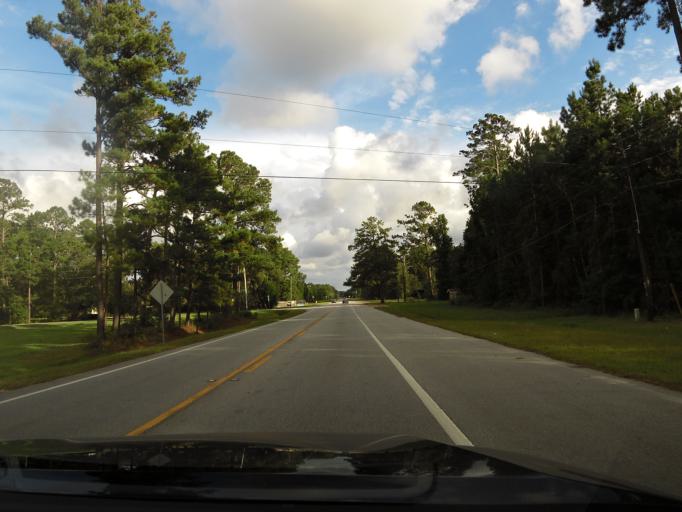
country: US
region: Georgia
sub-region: Liberty County
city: Midway
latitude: 31.7328
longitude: -81.4302
